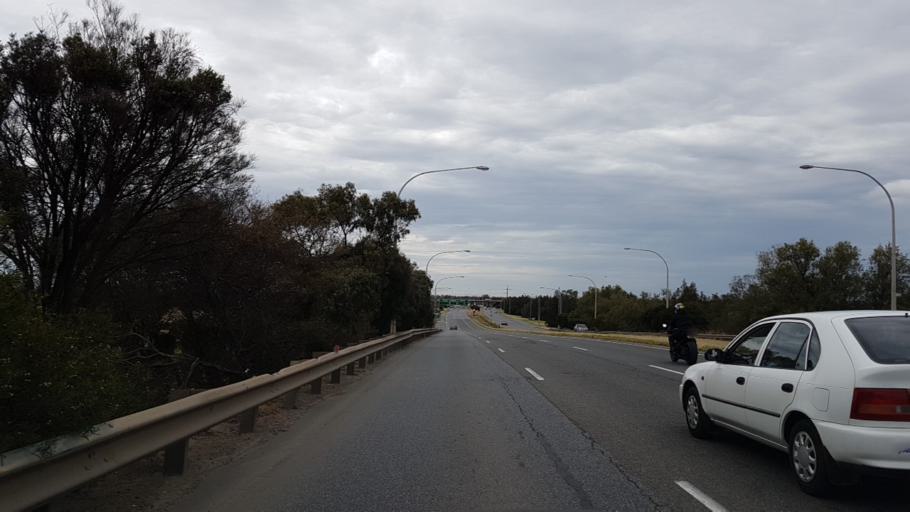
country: AU
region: South Australia
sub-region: Port Adelaide Enfield
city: Enfield
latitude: -34.8188
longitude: 138.5978
